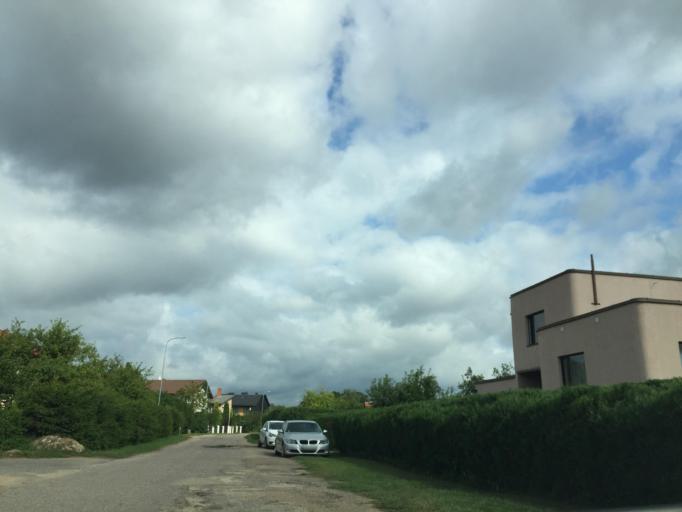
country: LV
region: Kegums
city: Kegums
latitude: 56.8013
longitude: 24.7426
